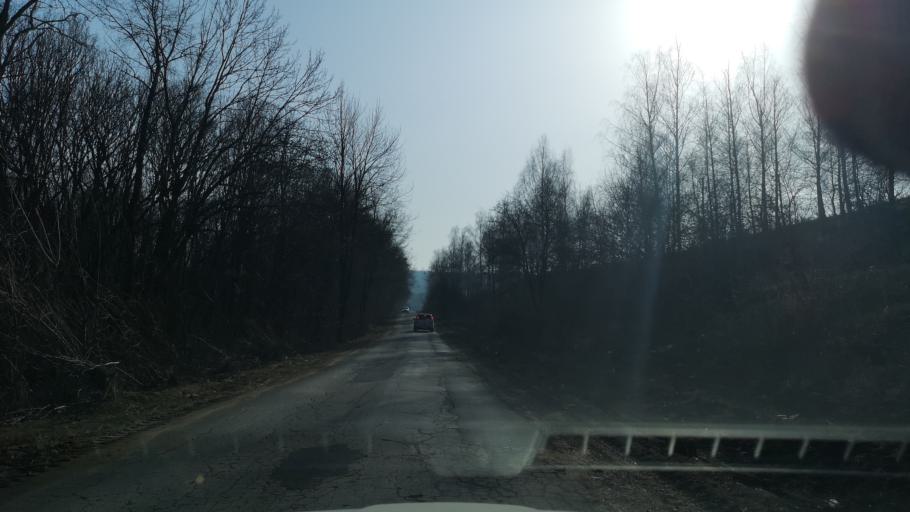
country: MD
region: Nisporeni
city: Nisporeni
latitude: 47.0946
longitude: 28.3155
